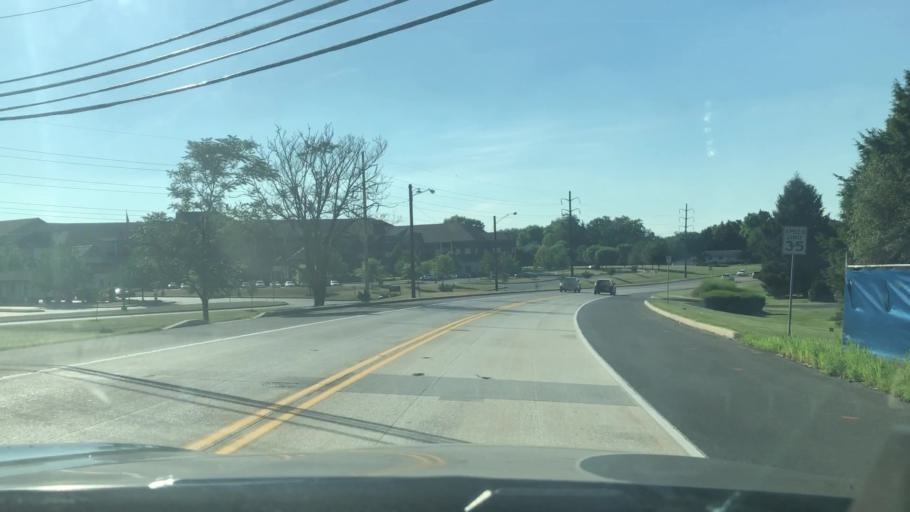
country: US
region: Pennsylvania
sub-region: Cumberland County
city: Shiremanstown
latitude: 40.2108
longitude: -76.9687
